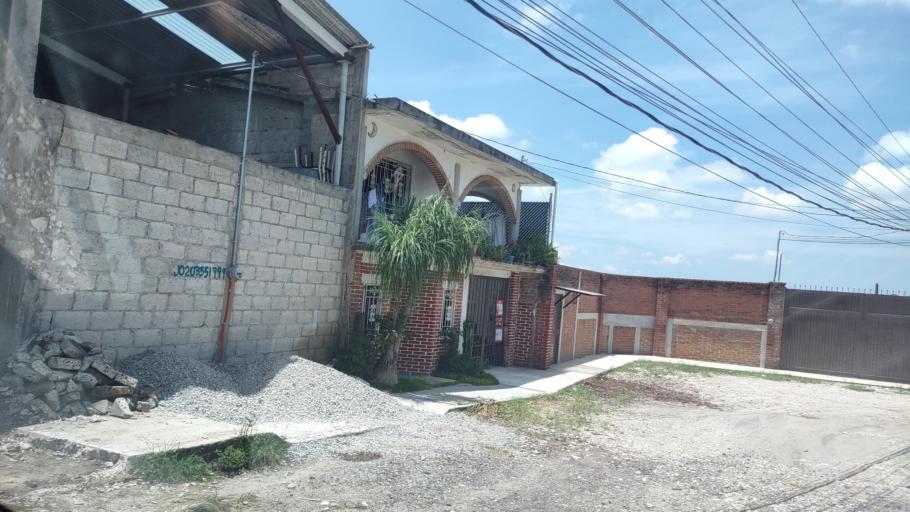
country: MX
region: Veracruz
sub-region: Emiliano Zapata
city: Dos Rios
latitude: 19.4928
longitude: -96.8133
